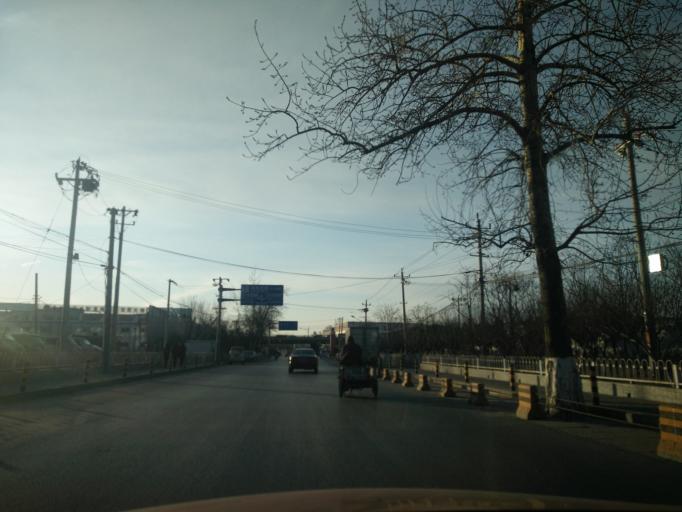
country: CN
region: Beijing
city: Huaxiang
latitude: 39.8207
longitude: 116.3414
